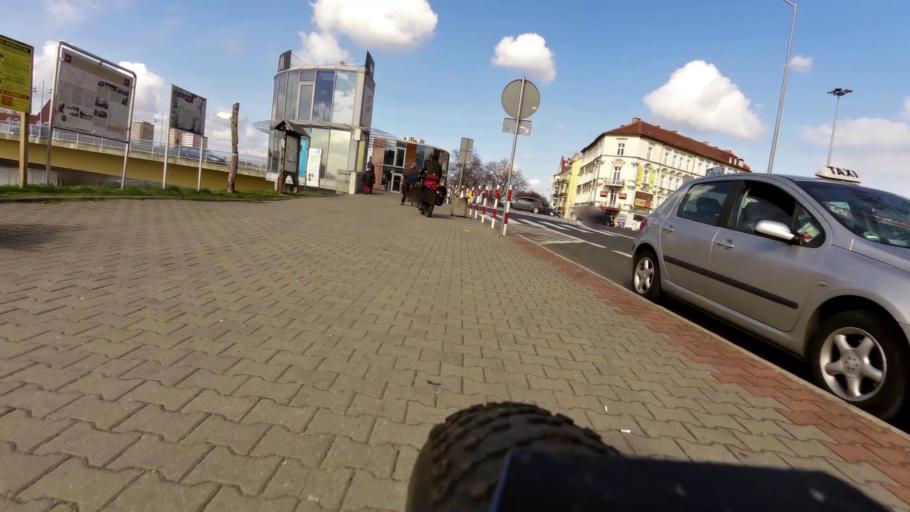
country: PL
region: Lubusz
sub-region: Powiat slubicki
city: Slubice
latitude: 52.3484
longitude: 14.5580
